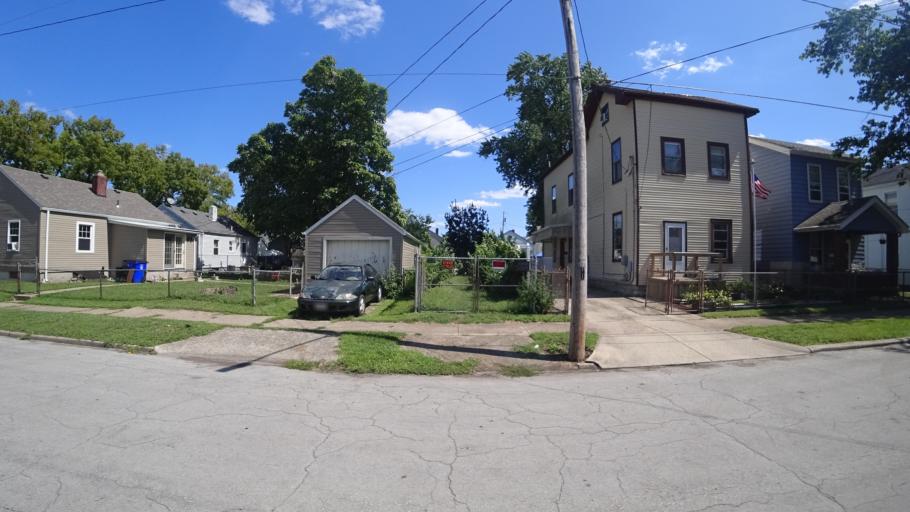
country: US
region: Ohio
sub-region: Butler County
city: Hamilton
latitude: 39.4050
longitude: -84.5526
